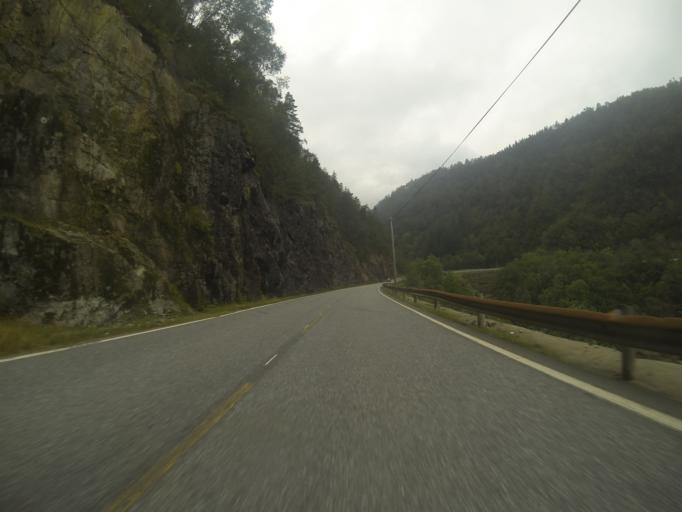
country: NO
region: Rogaland
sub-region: Suldal
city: Sand
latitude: 59.5373
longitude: 6.2545
